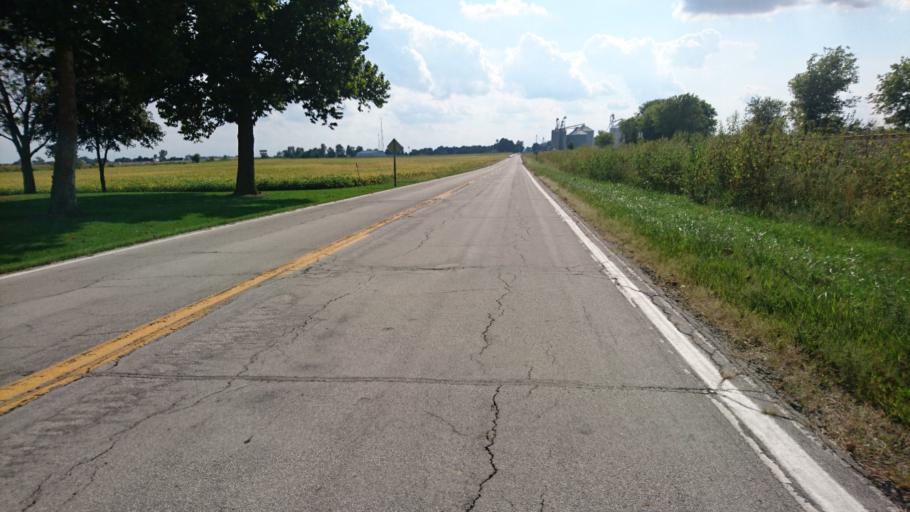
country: US
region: Illinois
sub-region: Logan County
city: Atlanta
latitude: 40.3251
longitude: -89.1573
